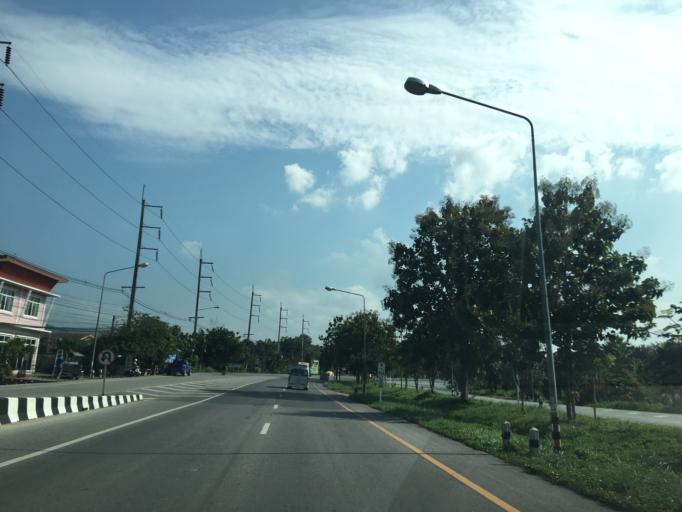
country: TH
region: Chiang Rai
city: Mae Lao
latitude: 19.7124
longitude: 99.7193
